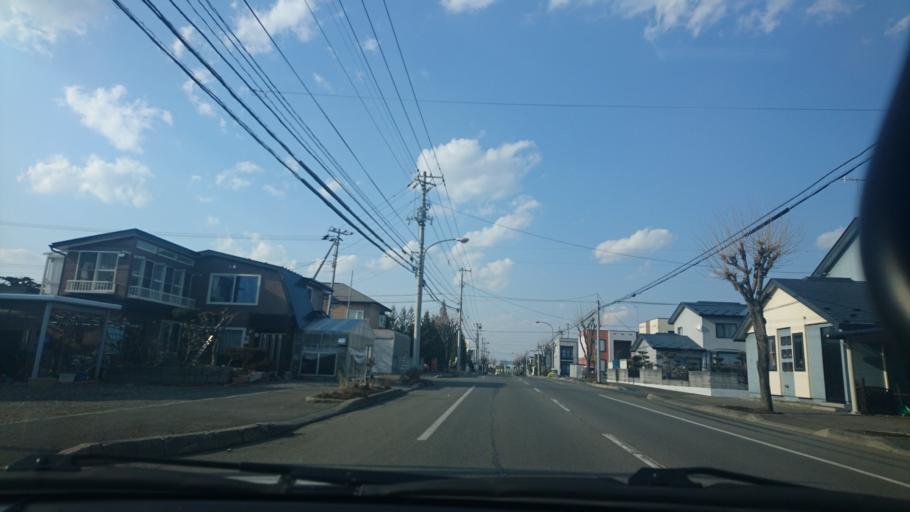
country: JP
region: Hokkaido
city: Obihiro
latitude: 42.9195
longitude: 143.1510
